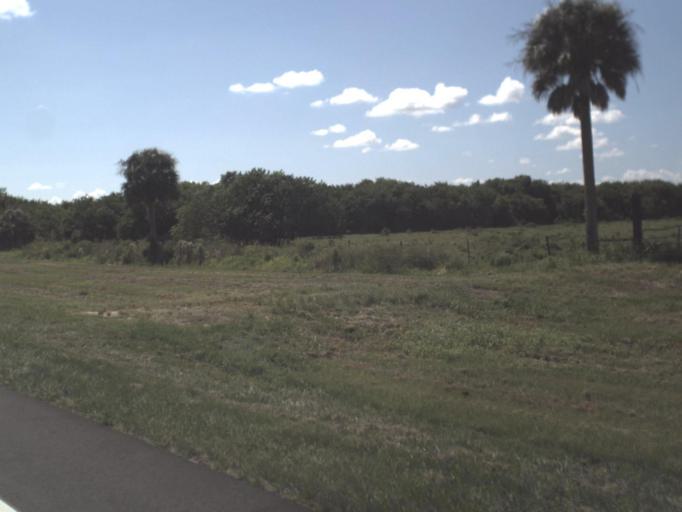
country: US
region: Florida
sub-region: Glades County
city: Buckhead Ridge
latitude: 27.0577
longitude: -80.9817
